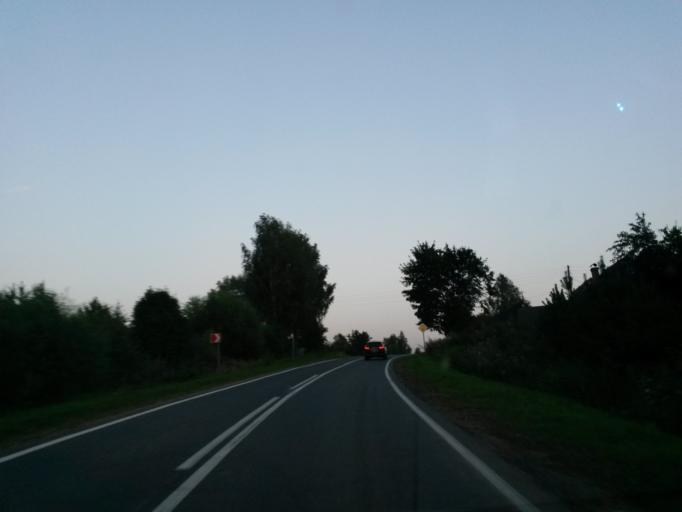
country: RU
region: Jaroslavl
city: Konstantinovskiy
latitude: 57.8056
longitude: 39.7633
